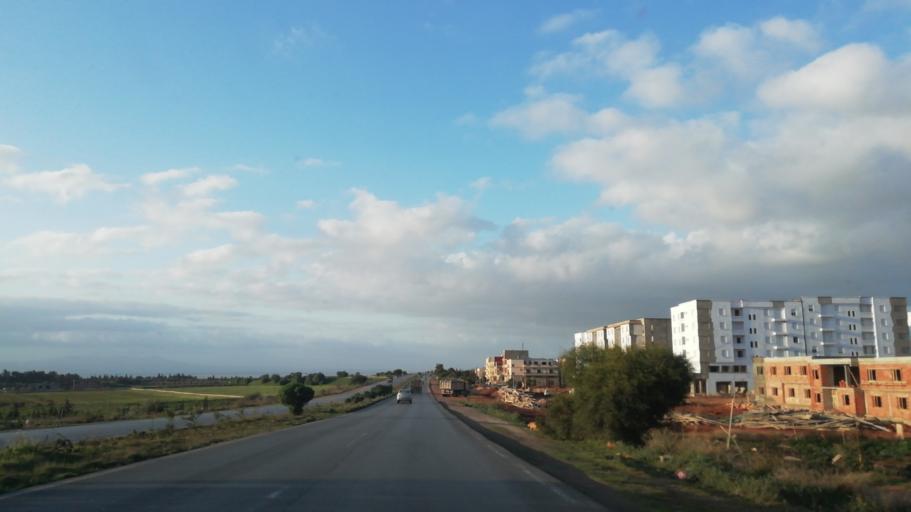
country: DZ
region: Oran
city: Es Senia
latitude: 35.6156
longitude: -0.7210
